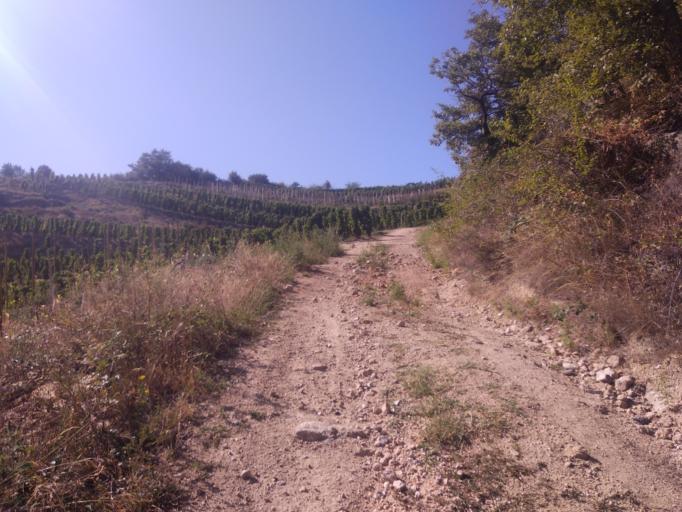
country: FR
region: Rhone-Alpes
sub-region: Departement de l'Ardeche
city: Sarras
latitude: 45.1957
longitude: 4.7814
